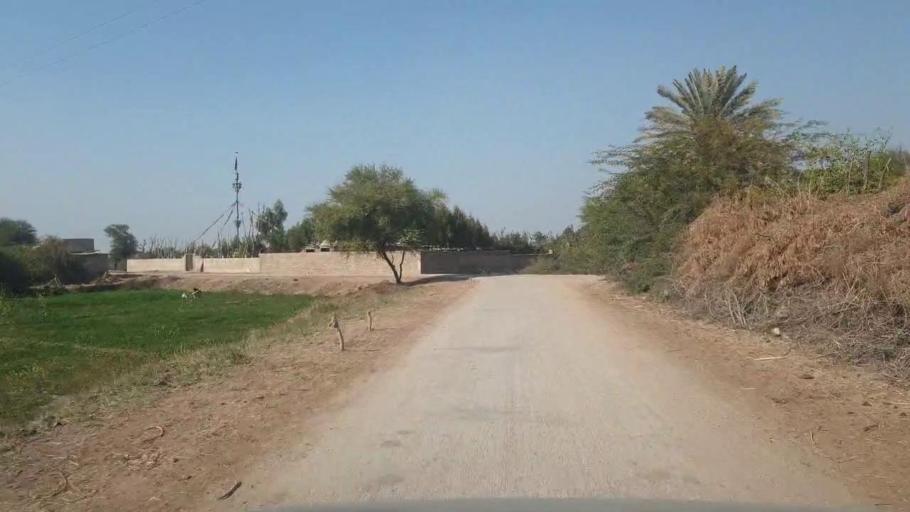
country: PK
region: Sindh
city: Chambar
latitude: 25.3161
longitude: 68.8419
